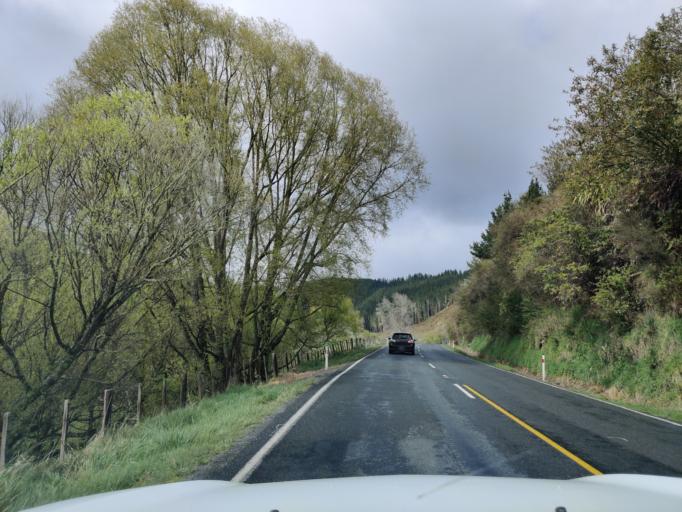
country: NZ
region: Waikato
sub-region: Otorohanga District
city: Otorohanga
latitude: -38.6124
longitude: 175.2187
